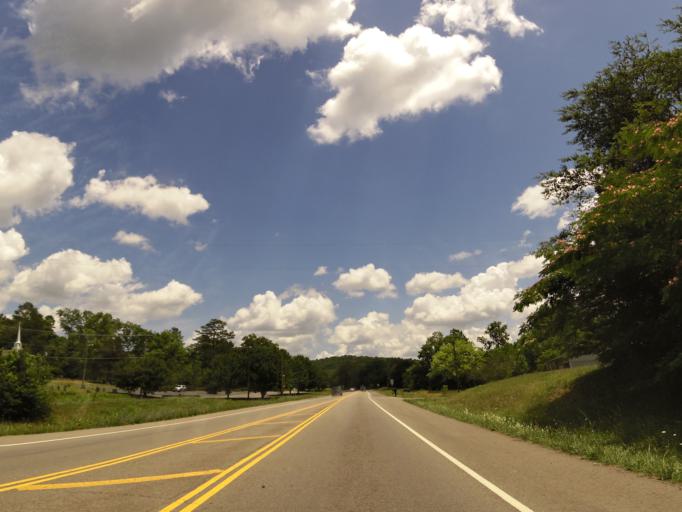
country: US
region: Tennessee
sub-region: Union County
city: Condon
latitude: 36.1903
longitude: -83.8932
